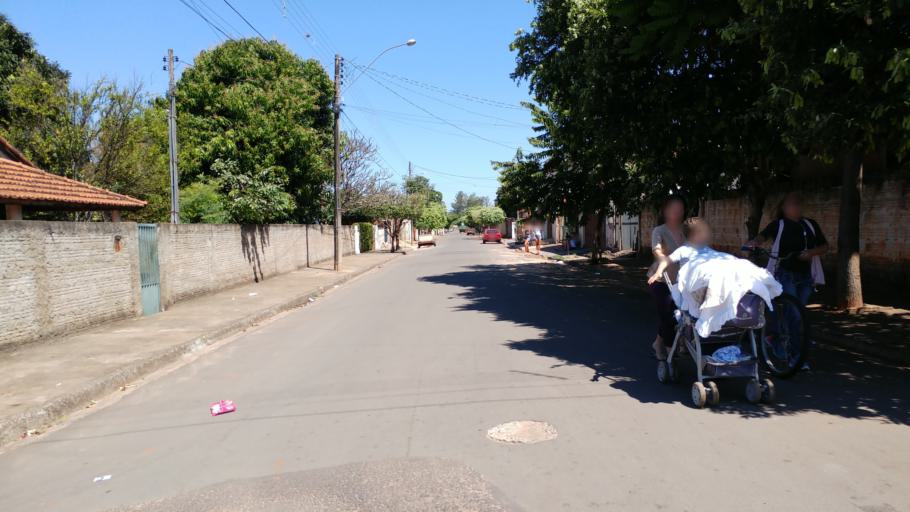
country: BR
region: Sao Paulo
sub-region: Paraguacu Paulista
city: Paraguacu Paulista
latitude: -22.4159
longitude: -50.5682
